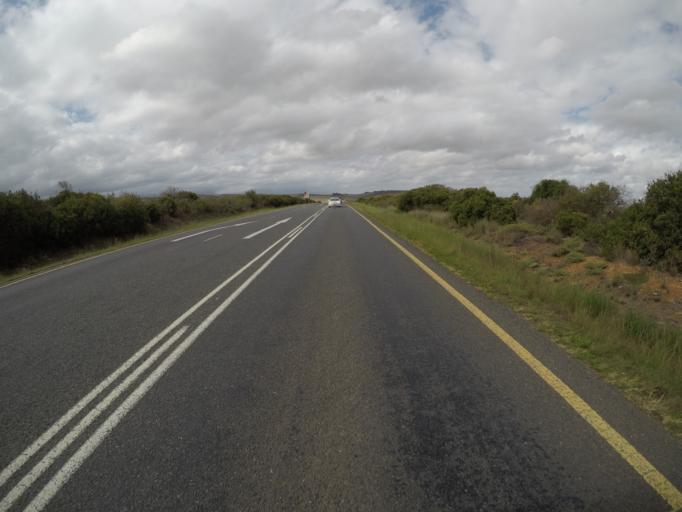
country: ZA
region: Western Cape
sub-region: Eden District Municipality
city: Riversdale
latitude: -34.1190
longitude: 21.1304
